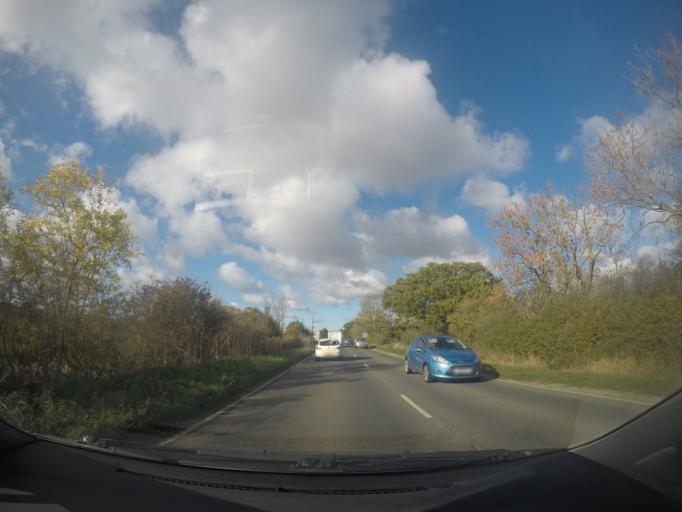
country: GB
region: England
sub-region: City of York
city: Nether Poppleton
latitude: 53.9816
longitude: -1.2030
